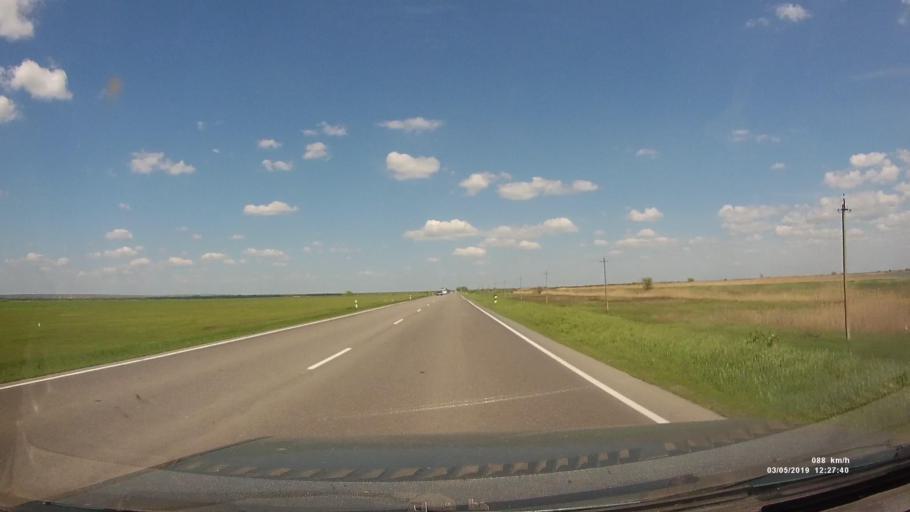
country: RU
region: Rostov
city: Semikarakorsk
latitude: 47.4623
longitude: 40.7227
